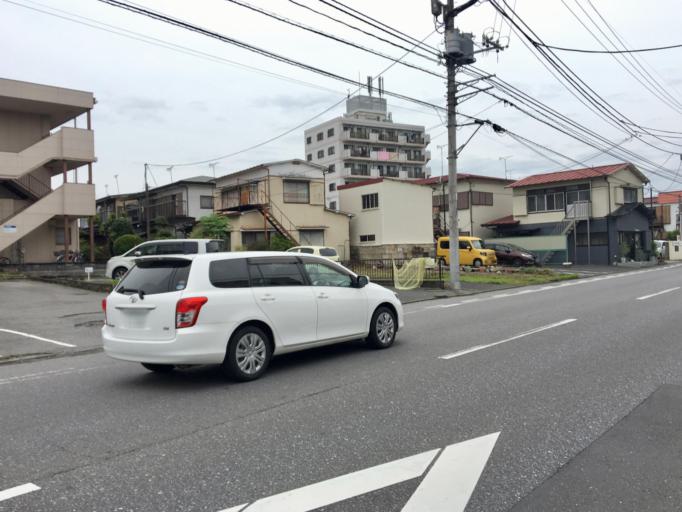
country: JP
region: Tochigi
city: Utsunomiya-shi
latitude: 36.5695
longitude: 139.8737
